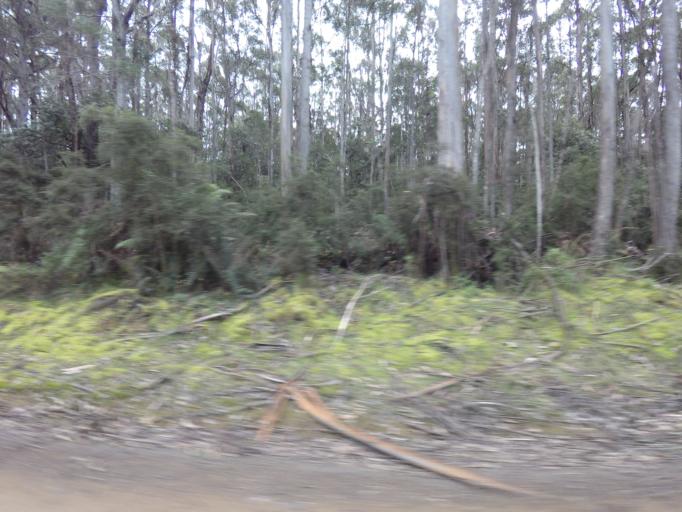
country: AU
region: Tasmania
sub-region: Huon Valley
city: Geeveston
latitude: -43.4232
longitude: 147.0094
